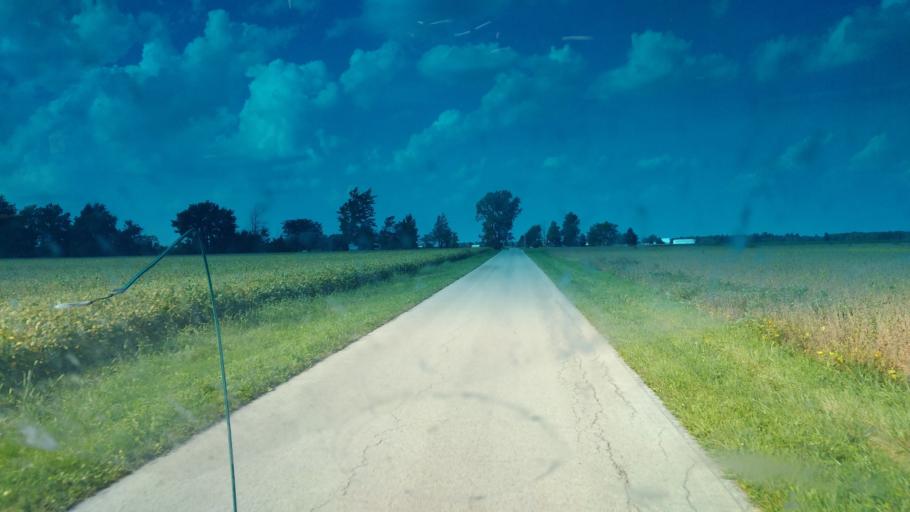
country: US
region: Ohio
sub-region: Hardin County
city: Forest
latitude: 40.8432
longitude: -83.5764
